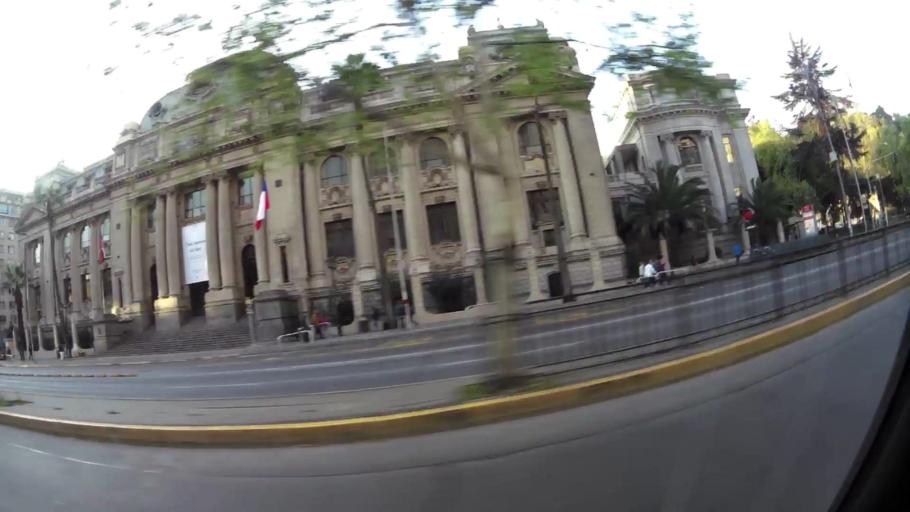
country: CL
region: Santiago Metropolitan
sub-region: Provincia de Santiago
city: Santiago
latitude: -33.4427
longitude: -70.6452
